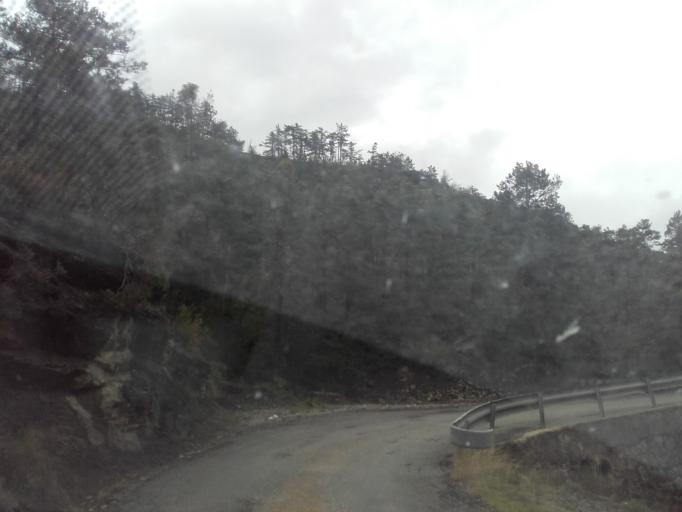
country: FR
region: Provence-Alpes-Cote d'Azur
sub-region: Departement des Alpes-de-Haute-Provence
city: Le Brusquet
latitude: 44.1336
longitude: 6.3310
